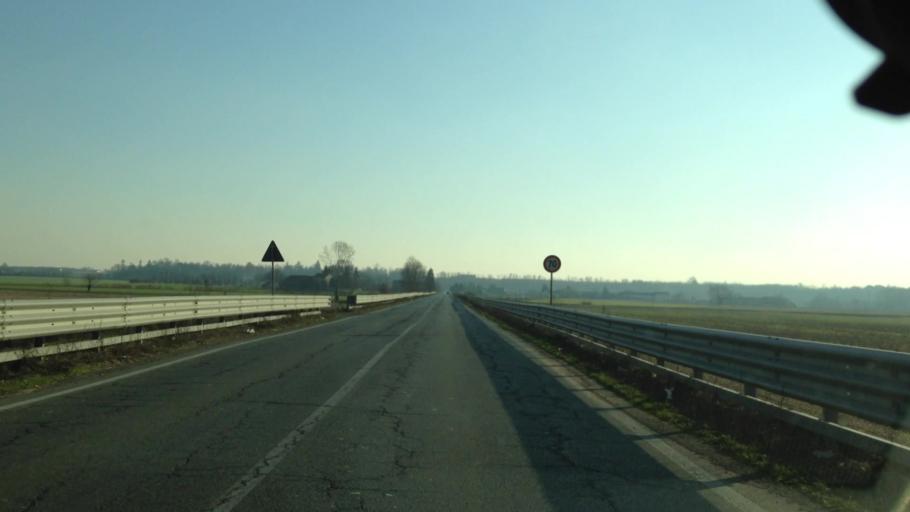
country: IT
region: Piedmont
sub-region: Provincia di Alessandria
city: Felizzano
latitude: 44.8873
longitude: 8.4407
